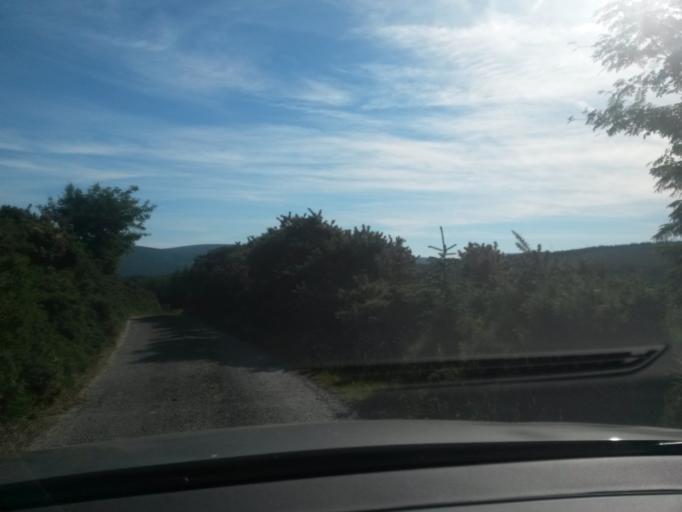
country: IE
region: Leinster
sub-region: Wicklow
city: Blessington
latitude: 53.1469
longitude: -6.4186
